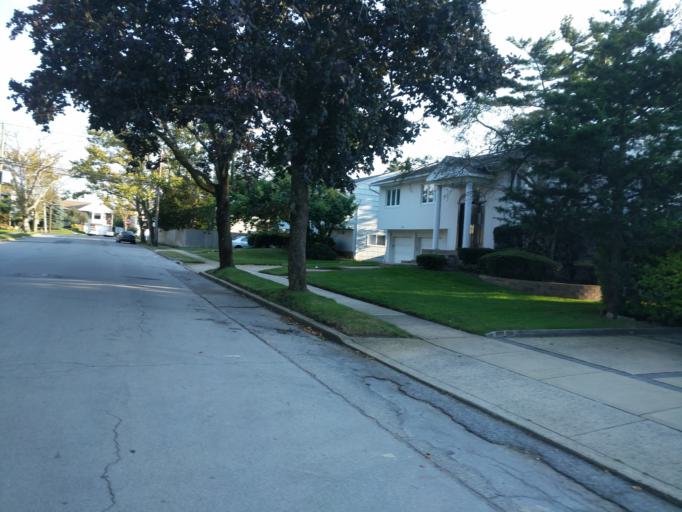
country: US
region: New York
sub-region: Nassau County
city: South Valley Stream
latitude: 40.6445
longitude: -73.7343
